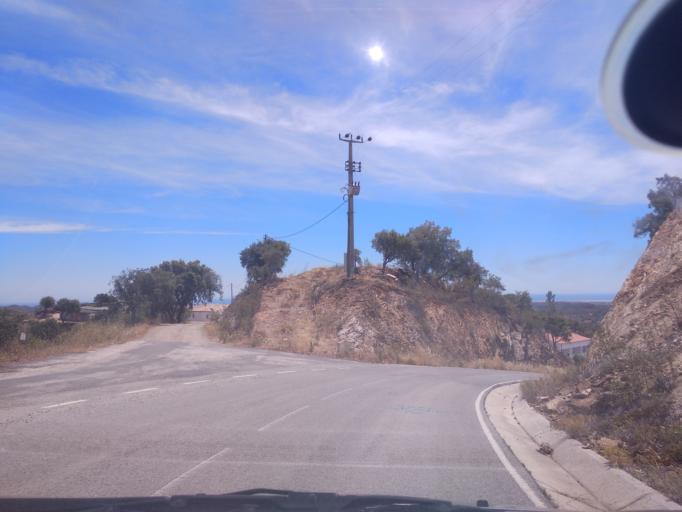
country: PT
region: Faro
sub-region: Sao Bras de Alportel
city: Sao Bras de Alportel
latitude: 37.1940
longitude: -7.7972
